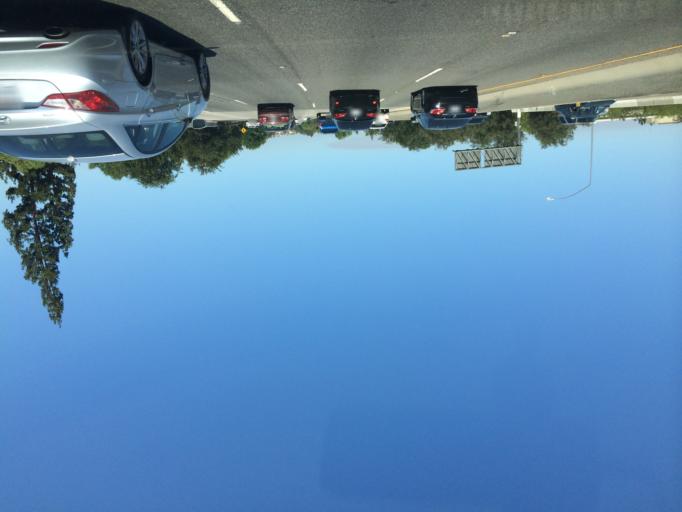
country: US
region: California
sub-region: Los Angeles County
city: Woodland Hills
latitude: 34.1708
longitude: -118.6066
